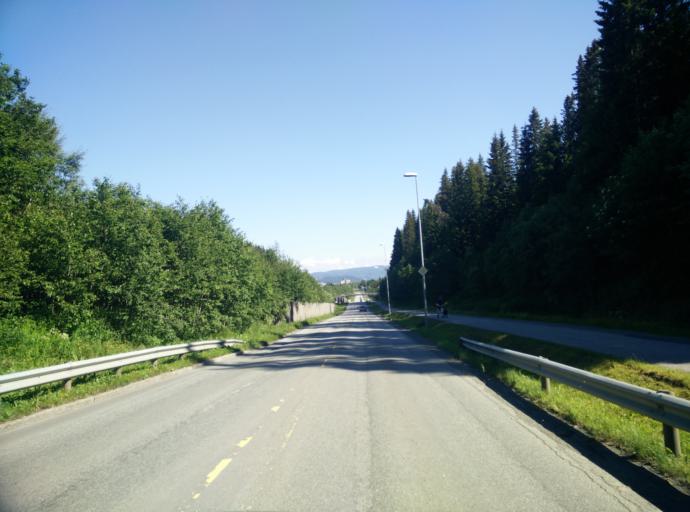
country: NO
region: Sor-Trondelag
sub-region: Trondheim
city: Trondheim
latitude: 63.3753
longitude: 10.3234
